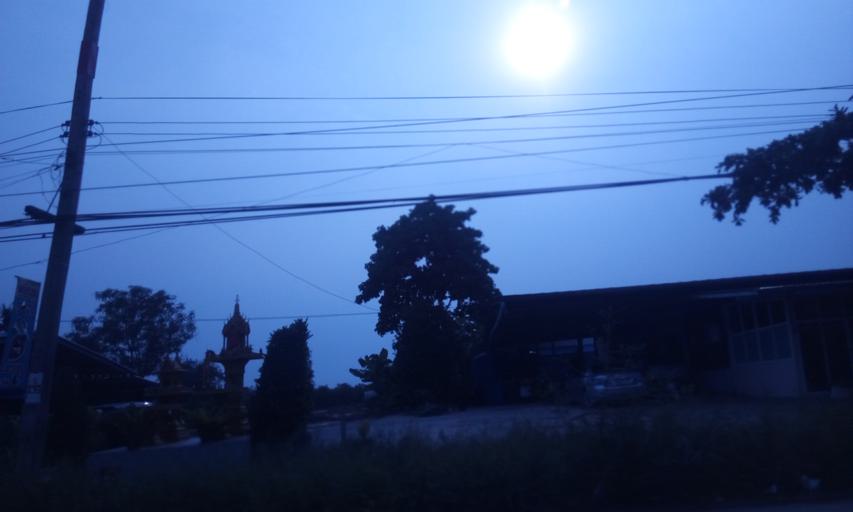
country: TH
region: Chachoengsao
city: Ban Pho
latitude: 13.6178
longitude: 101.1109
